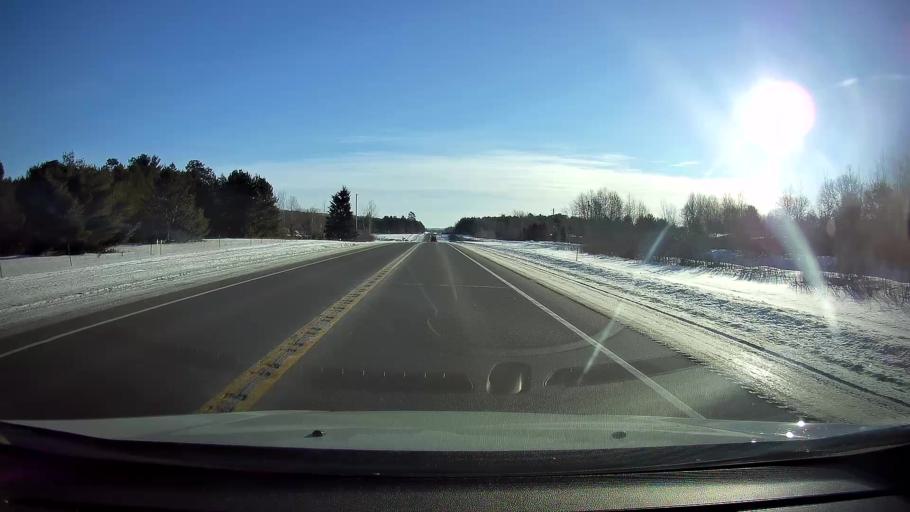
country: US
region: Wisconsin
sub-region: Sawyer County
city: Hayward
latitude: 45.9854
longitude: -91.5833
